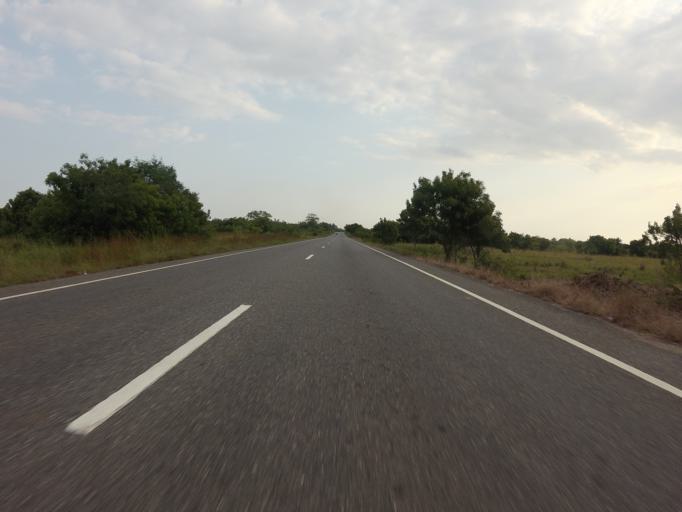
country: GH
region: Volta
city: Ho
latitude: 6.1169
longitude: 0.5191
